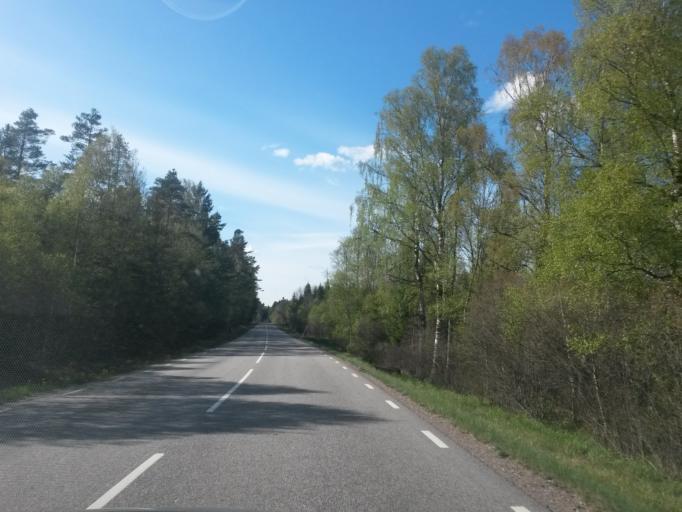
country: SE
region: Vaestra Goetaland
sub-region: Herrljunga Kommun
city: Herrljunga
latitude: 57.9388
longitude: 13.0240
